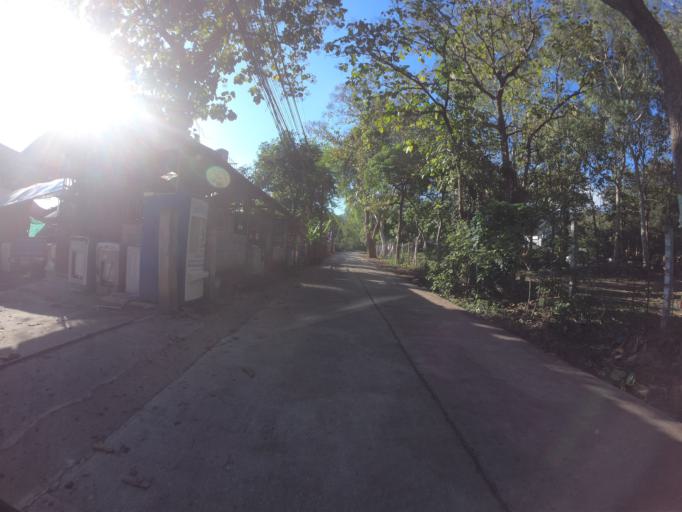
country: TH
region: Chiang Mai
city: Chiang Mai
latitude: 18.7705
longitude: 98.9437
